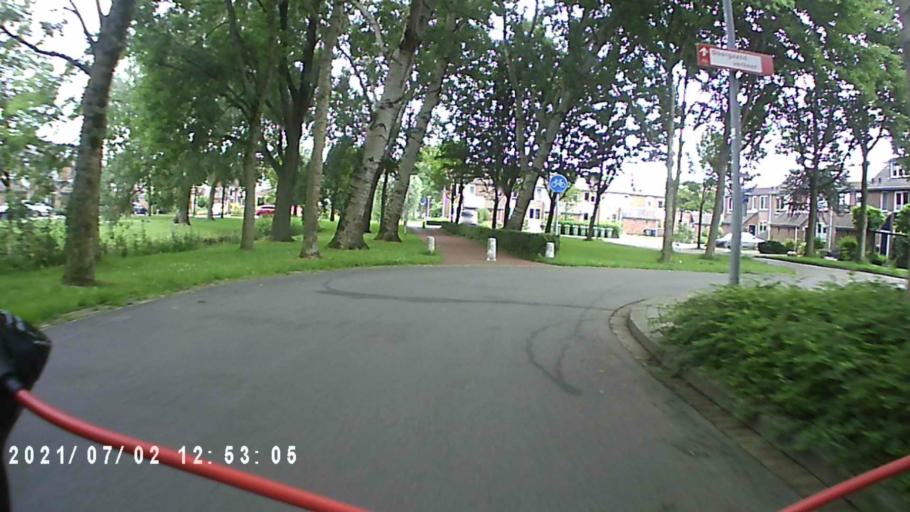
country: NL
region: Groningen
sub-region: Gemeente Groningen
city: Oosterpark
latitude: 53.2327
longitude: 6.5960
